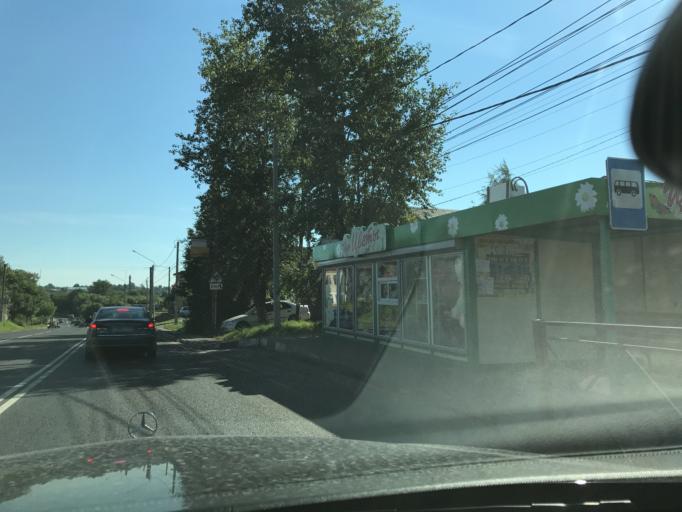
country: RU
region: Vladimir
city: Kirzhach
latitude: 56.1543
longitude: 38.8571
